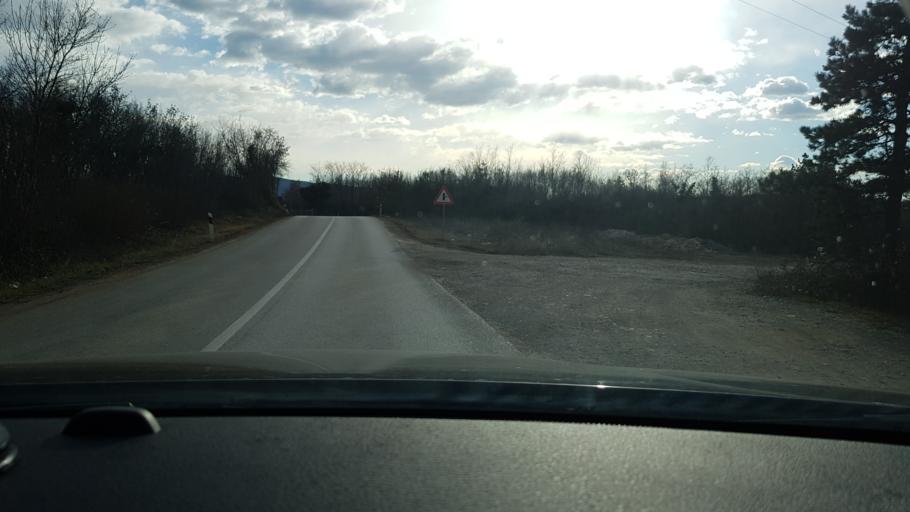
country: HR
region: Istarska
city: Vinez
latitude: 45.1161
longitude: 14.1101
